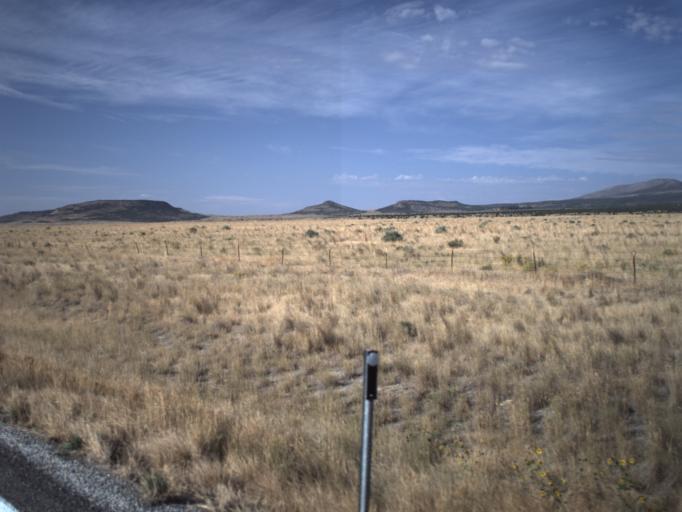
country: US
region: Idaho
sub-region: Oneida County
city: Malad City
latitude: 41.8888
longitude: -113.1131
